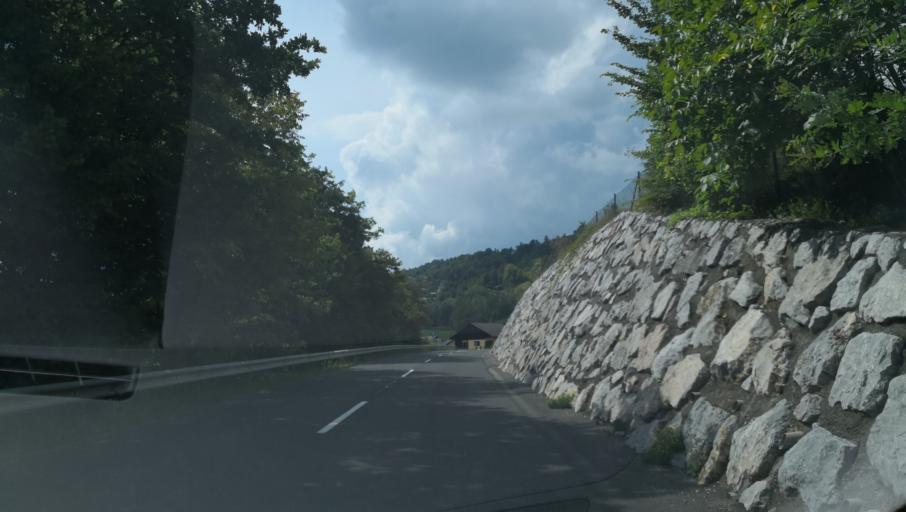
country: SI
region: Zuzemberk
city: Zuzemberk
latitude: 45.8550
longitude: 14.8844
